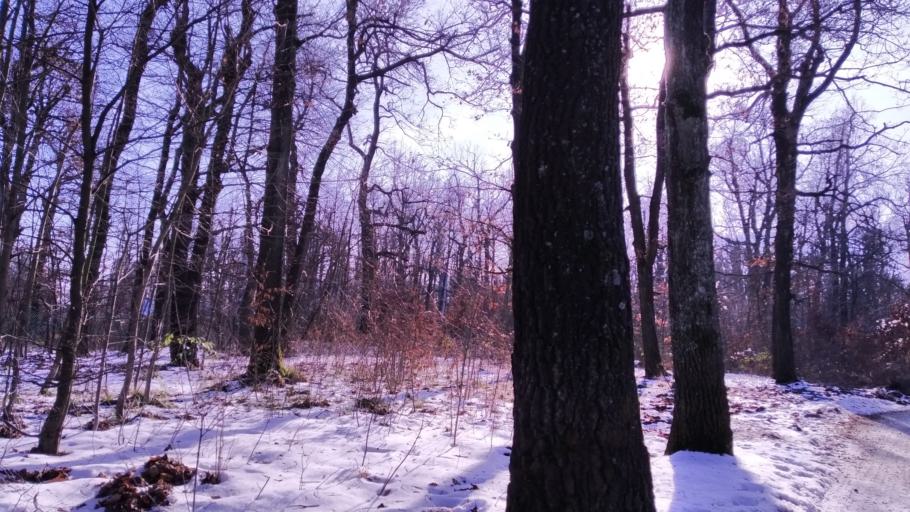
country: HU
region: Pest
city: Pilisszentkereszt
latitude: 47.7169
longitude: 18.8973
